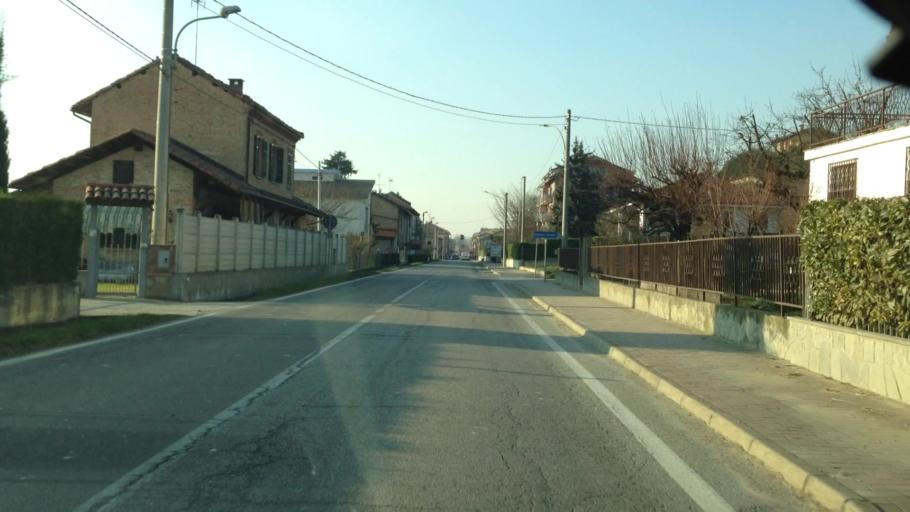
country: IT
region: Piedmont
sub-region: Provincia di Asti
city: Montegrosso
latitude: 44.8173
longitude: 8.2476
